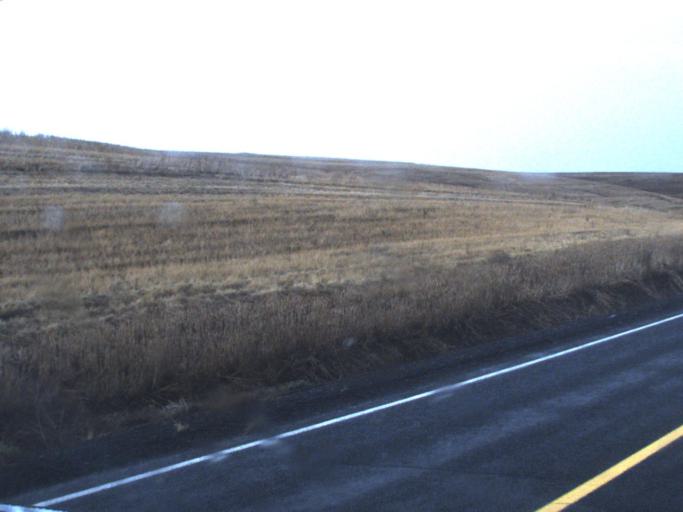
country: US
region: Washington
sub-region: Spokane County
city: Cheney
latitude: 47.2023
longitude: -117.8836
